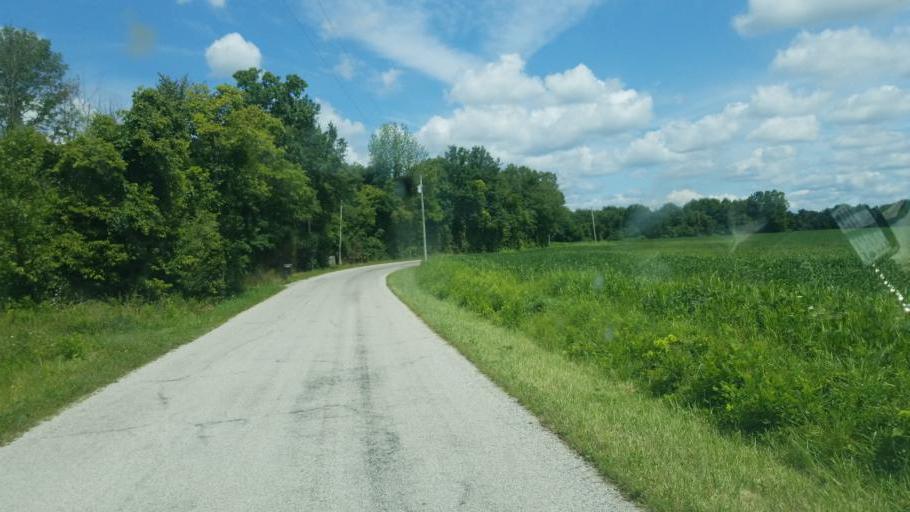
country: US
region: Ohio
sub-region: Delaware County
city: Sunbury
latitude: 40.2864
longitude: -82.8295
